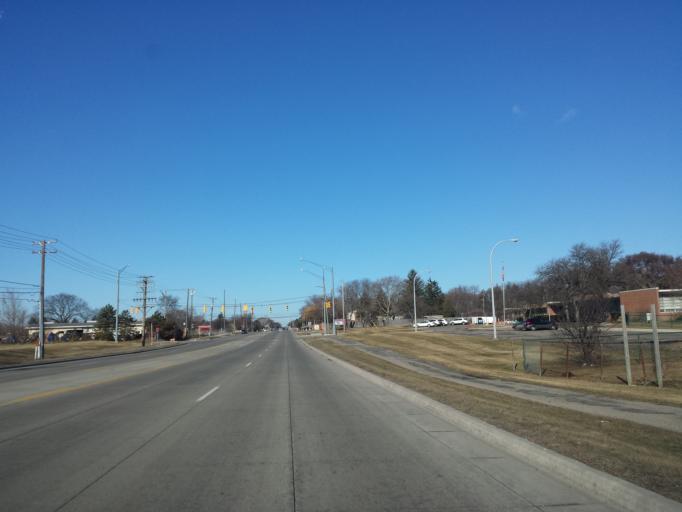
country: US
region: Michigan
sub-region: Oakland County
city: Lathrup Village
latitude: 42.5022
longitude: -83.2320
